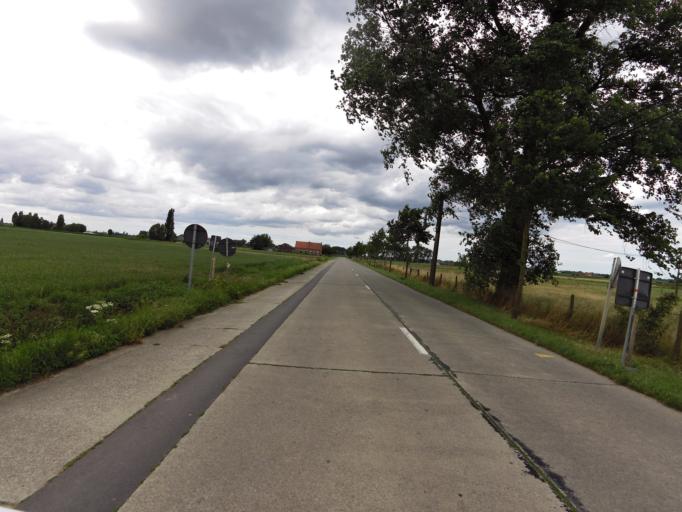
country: BE
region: Flanders
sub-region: Provincie West-Vlaanderen
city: Hooglede
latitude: 50.9907
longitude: 3.0548
